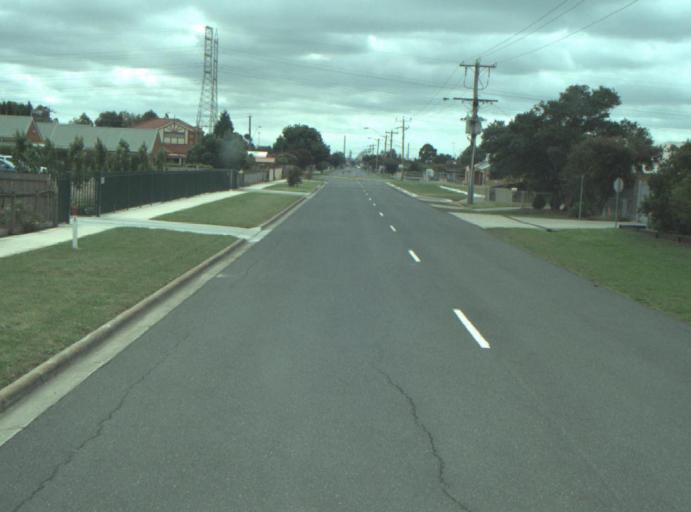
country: AU
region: Victoria
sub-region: Greater Geelong
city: Bell Post Hill
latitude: -38.0715
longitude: 144.3370
